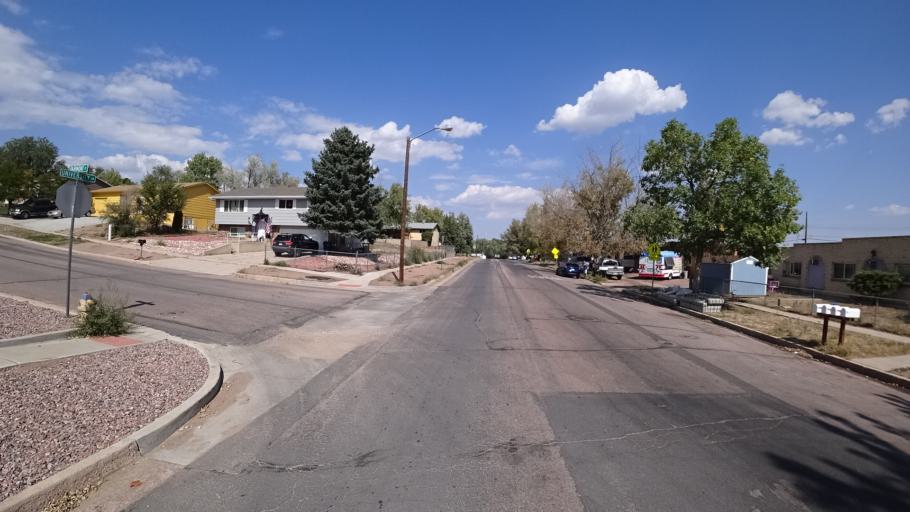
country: US
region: Colorado
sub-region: El Paso County
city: Stratmoor
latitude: 38.8299
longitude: -104.7627
